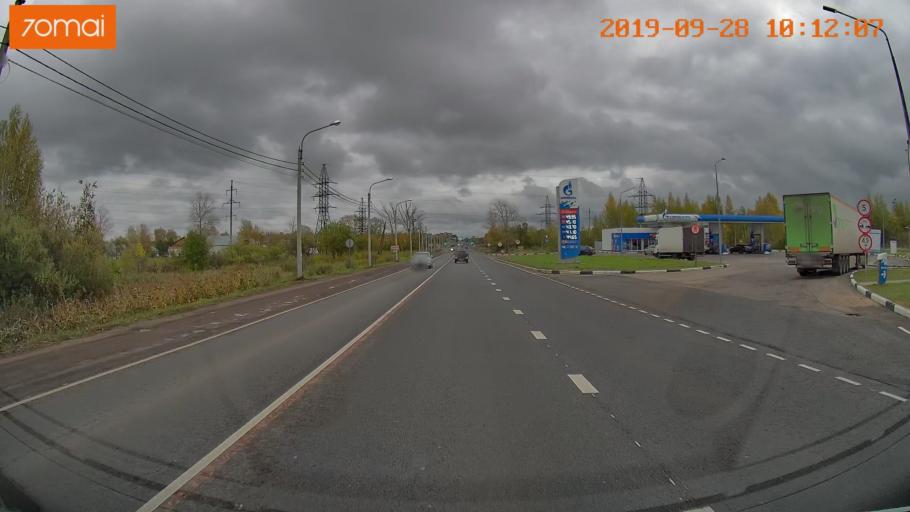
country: RU
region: Jaroslavl
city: Yaroslavl
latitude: 57.5426
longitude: 39.9506
